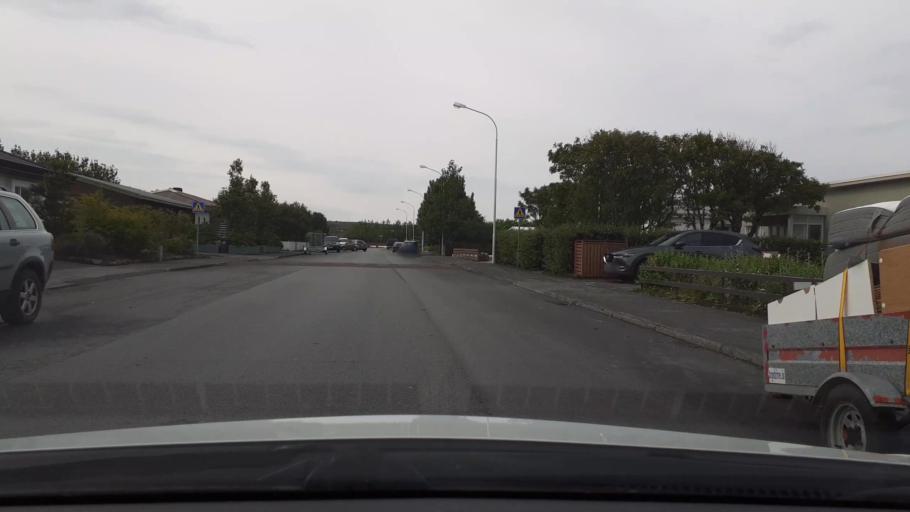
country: IS
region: Southern Peninsula
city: Reykjanesbaer
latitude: 63.9870
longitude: -22.5538
